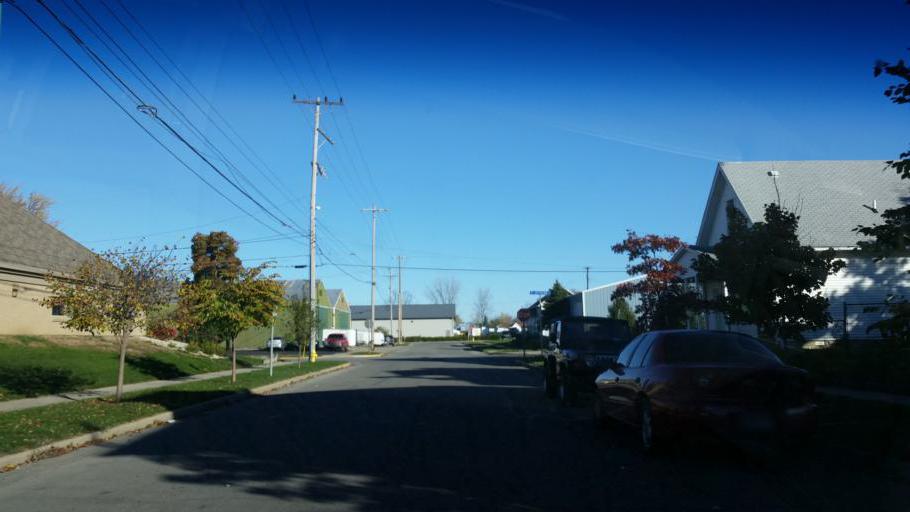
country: US
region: Indiana
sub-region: Howard County
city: Kokomo
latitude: 40.4905
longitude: -86.1289
